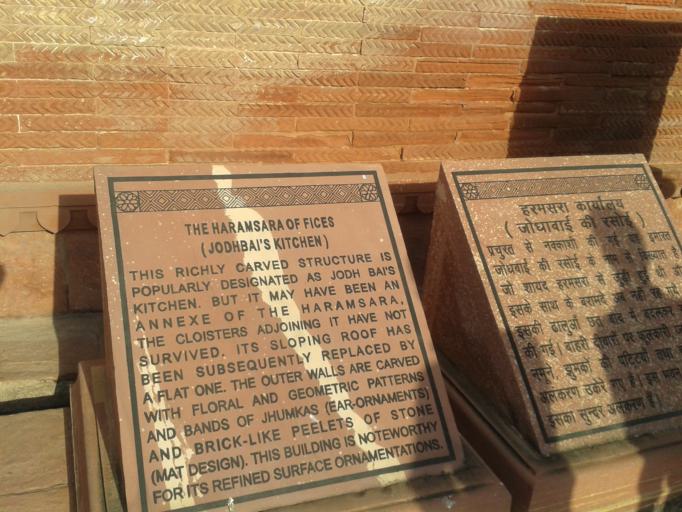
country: IN
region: Uttar Pradesh
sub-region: Agra
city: Fatehpur Sikri
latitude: 27.0967
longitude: 77.6655
